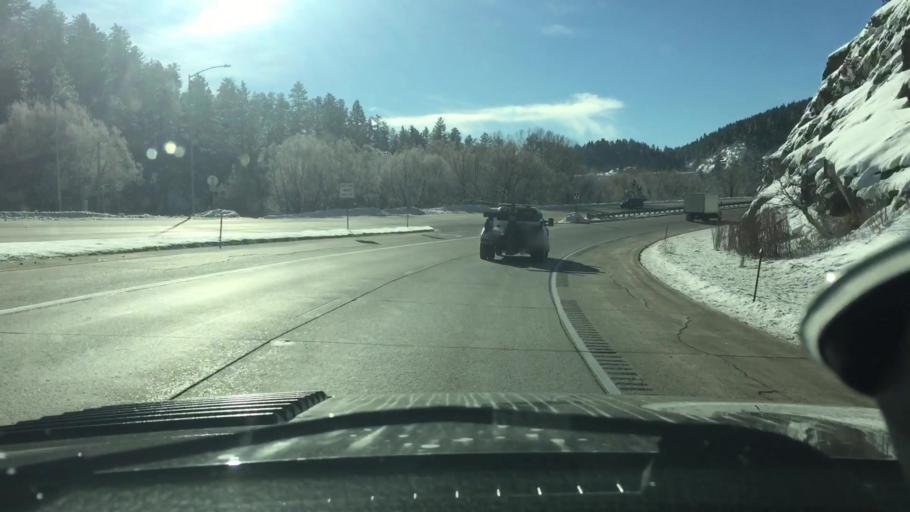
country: US
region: Colorado
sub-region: Jefferson County
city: Indian Hills
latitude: 39.6125
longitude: -105.2315
